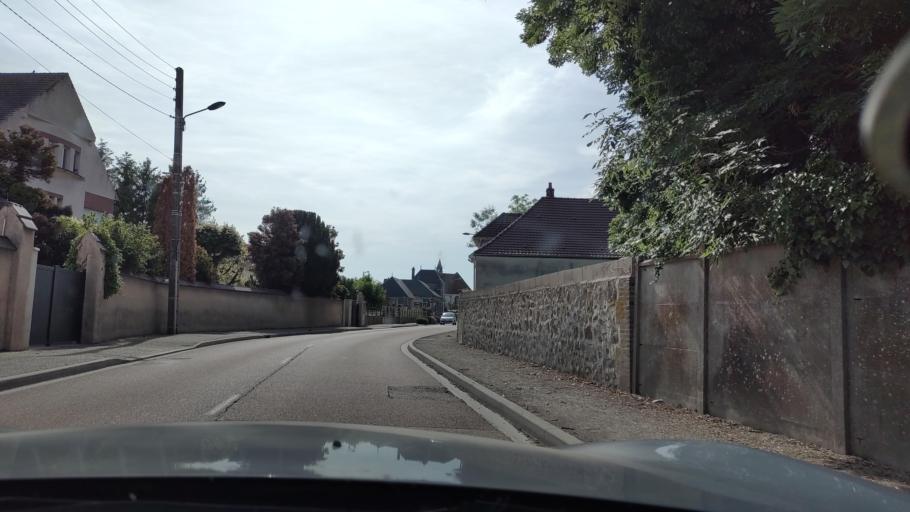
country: FR
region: Champagne-Ardenne
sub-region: Departement de l'Aube
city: Marigny-le-Chatel
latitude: 48.4040
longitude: 3.7338
